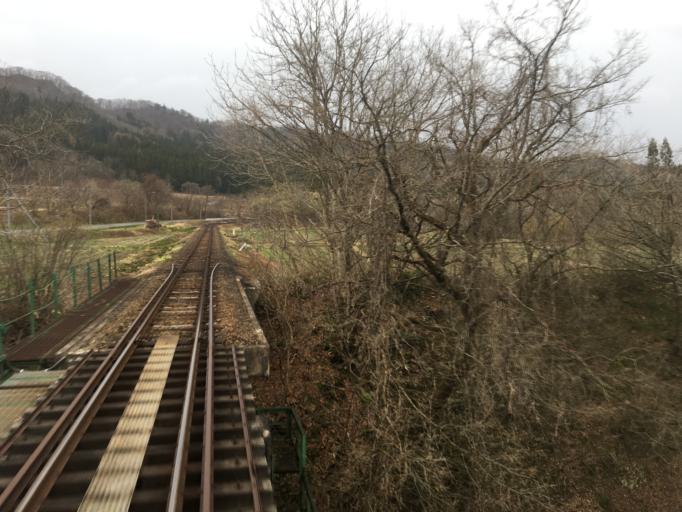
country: JP
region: Akita
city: Takanosu
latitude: 39.9270
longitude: 140.4173
